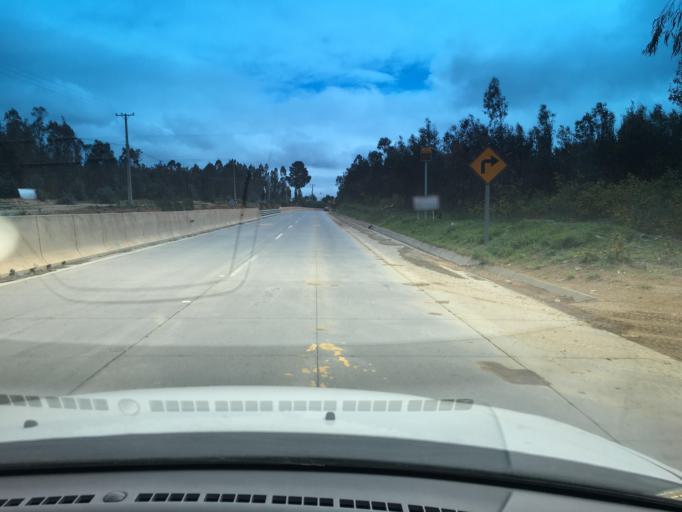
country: CL
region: Valparaiso
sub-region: Provincia de Valparaiso
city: Valparaiso
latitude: -33.0944
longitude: -71.5957
